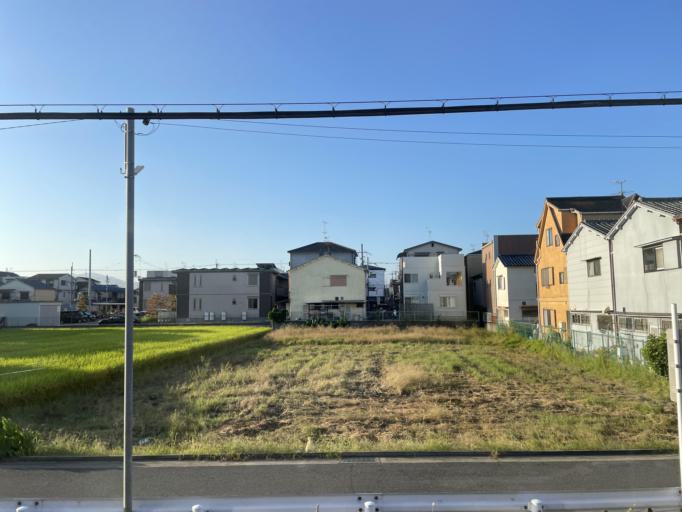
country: JP
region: Osaka
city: Matsubara
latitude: 34.5710
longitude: 135.5796
